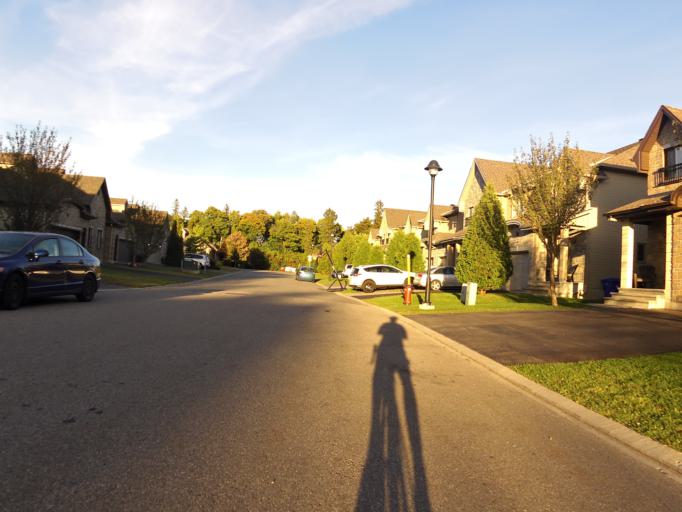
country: CA
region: Ontario
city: Ottawa
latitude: 45.4108
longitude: -75.7735
